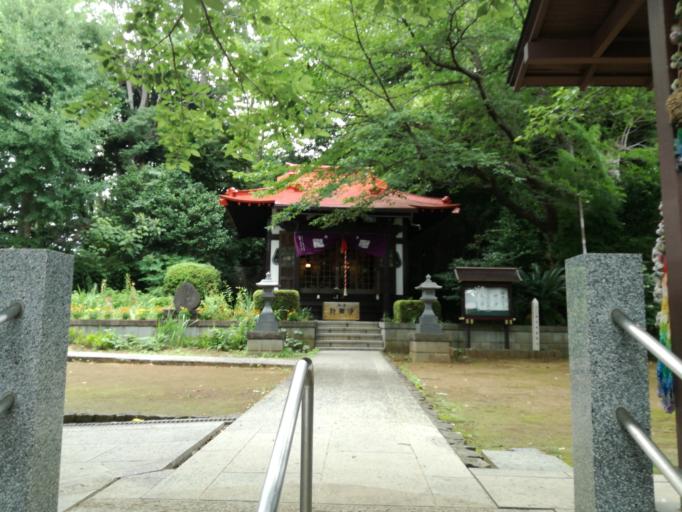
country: JP
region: Kanagawa
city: Yokohama
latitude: 35.4368
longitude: 139.5670
